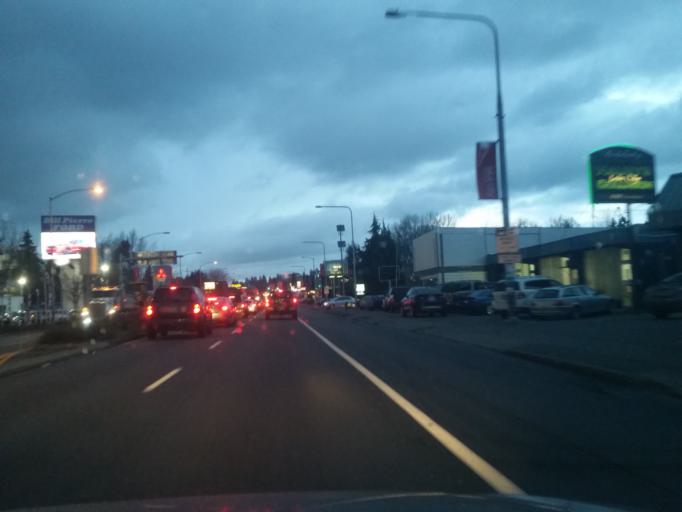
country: US
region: Washington
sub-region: King County
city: Lake Forest Park
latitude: 47.7124
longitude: -122.2993
